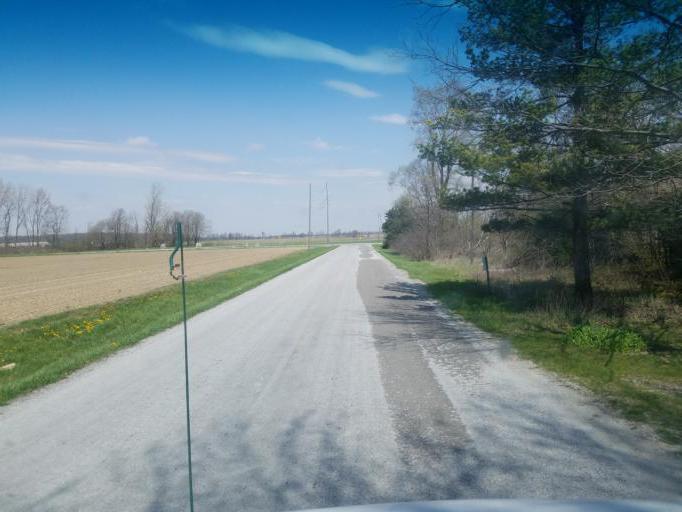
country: US
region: Ohio
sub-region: Hardin County
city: Forest
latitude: 40.7587
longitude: -83.5378
